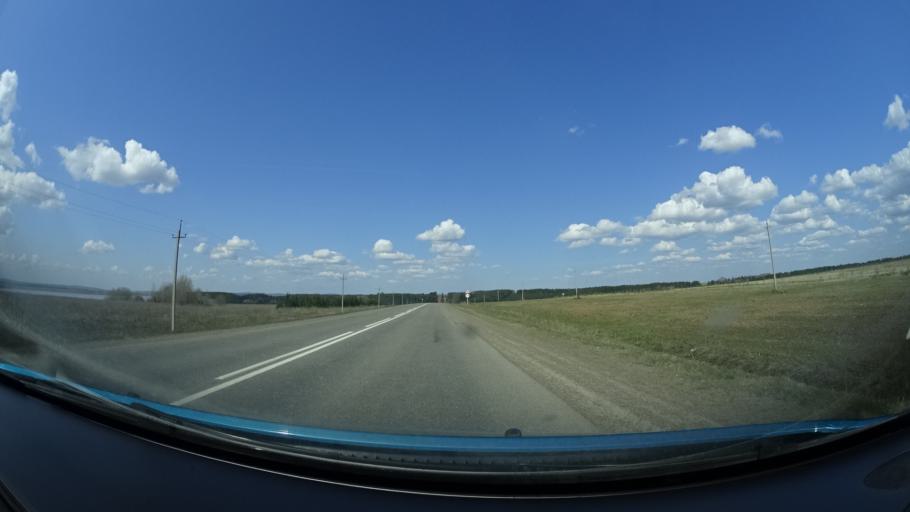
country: RU
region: Perm
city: Osa
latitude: 57.2449
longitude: 55.5925
